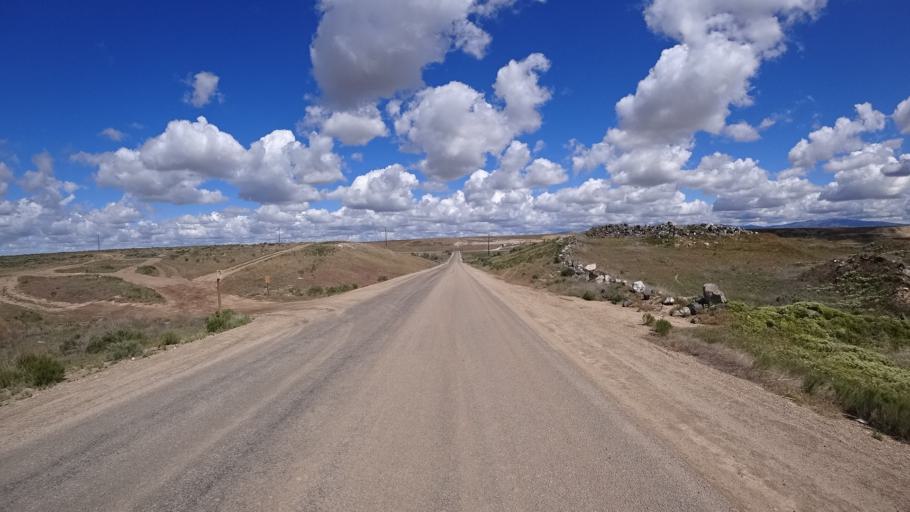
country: US
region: Idaho
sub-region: Ada County
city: Garden City
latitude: 43.4868
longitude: -116.2743
